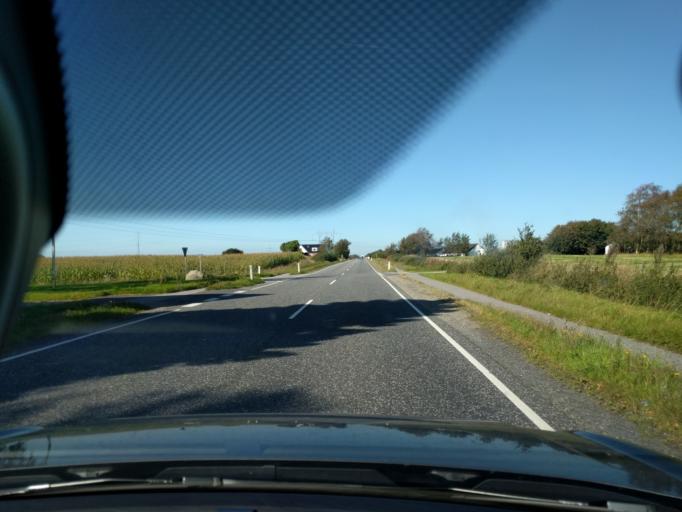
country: DK
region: North Denmark
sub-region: Vesthimmerland Kommune
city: Alestrup
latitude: 56.7179
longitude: 9.6121
